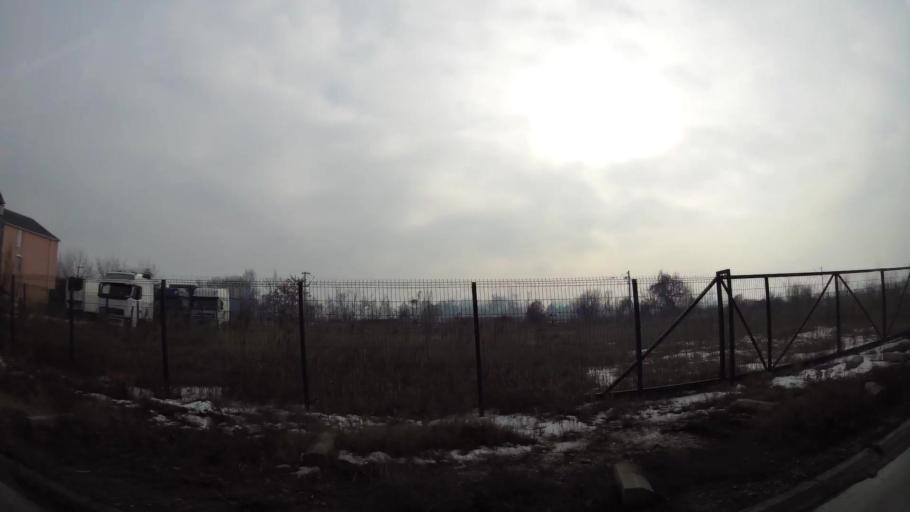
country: MK
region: Ilinden
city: Ilinden
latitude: 41.9949
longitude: 21.5529
